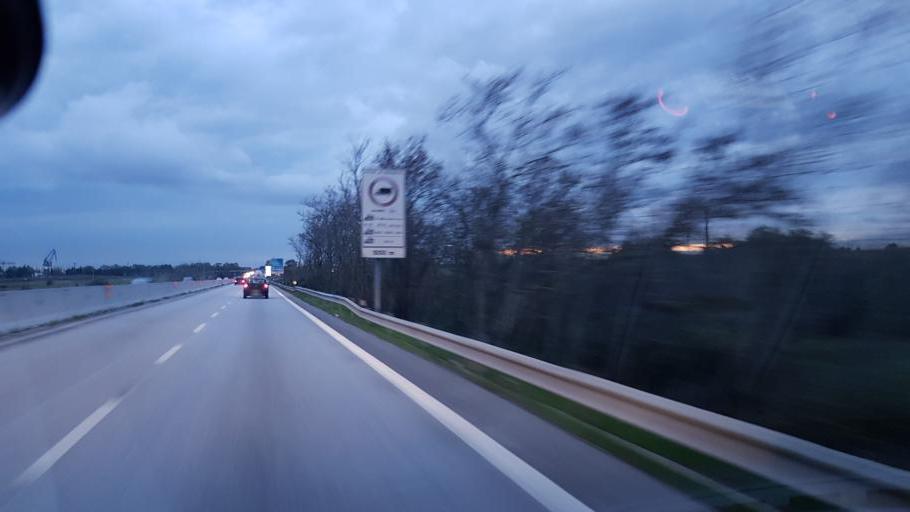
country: IT
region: Apulia
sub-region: Provincia di Taranto
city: Paolo VI
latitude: 40.5083
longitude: 17.2758
